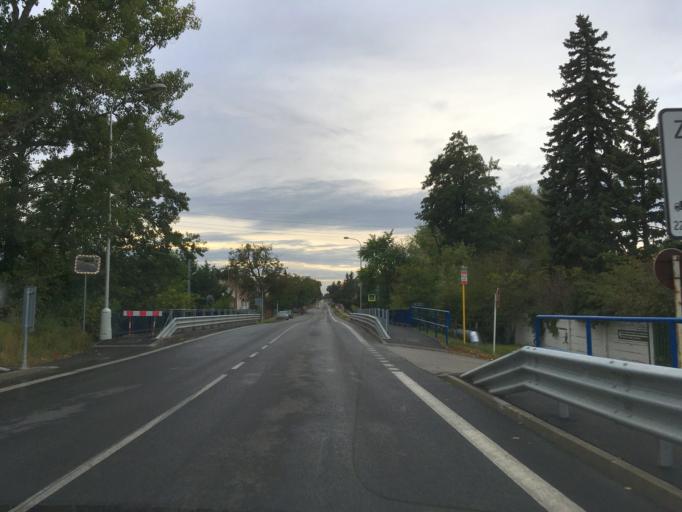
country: SK
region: Nitriansky
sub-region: Okres Nove Zamky
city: Nove Zamky
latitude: 47.9964
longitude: 18.1850
